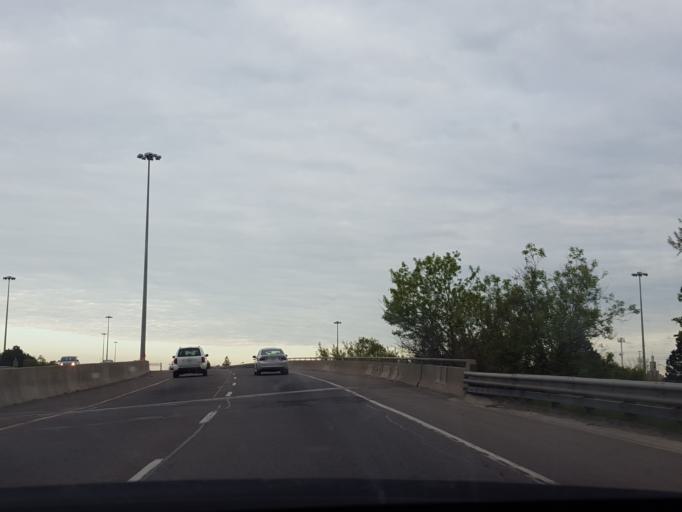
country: CA
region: Ontario
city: Etobicoke
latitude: 43.7109
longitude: -79.5030
